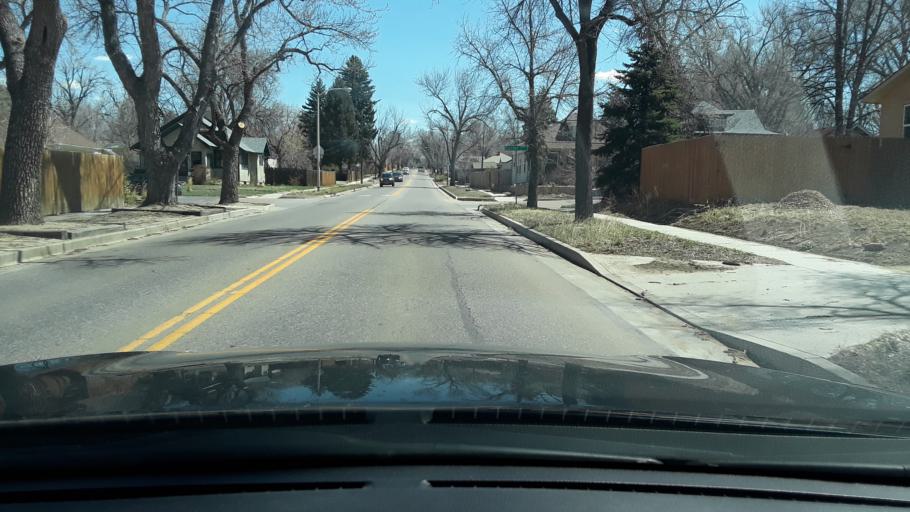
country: US
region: Colorado
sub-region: El Paso County
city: Colorado Springs
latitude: 38.8501
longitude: -104.8064
